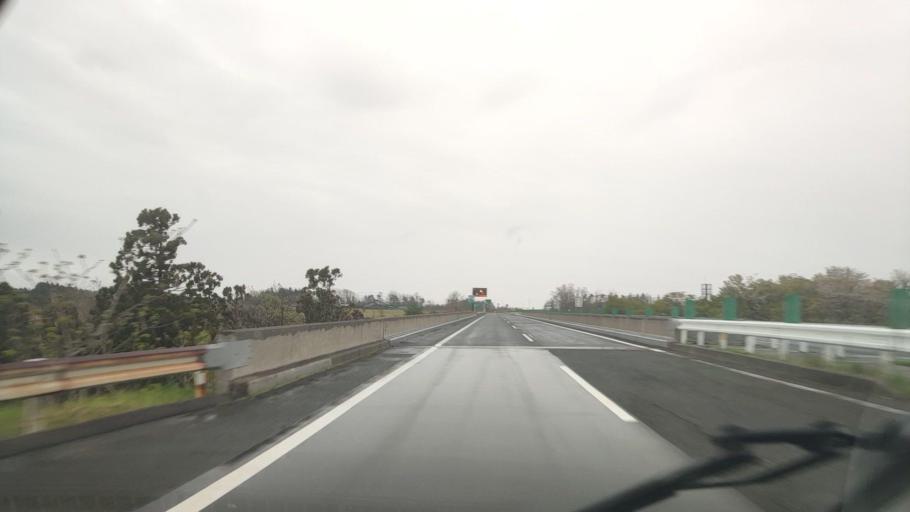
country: JP
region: Akita
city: Noshiromachi
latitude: 40.1259
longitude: 140.0124
